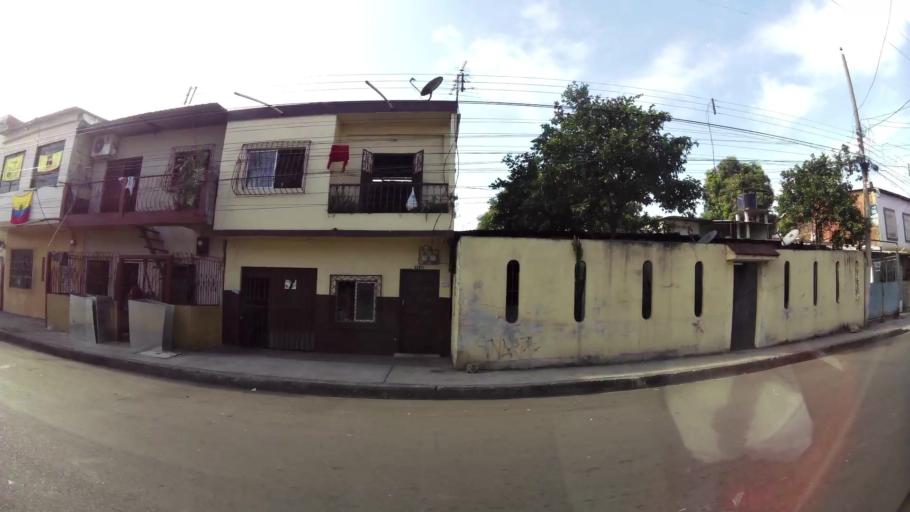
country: EC
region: Guayas
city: Guayaquil
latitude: -2.1922
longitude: -79.9214
